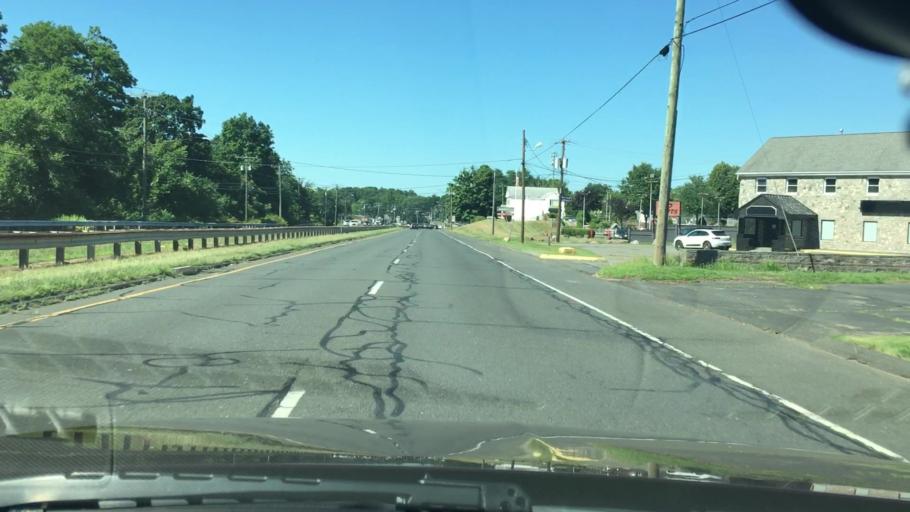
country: US
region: Connecticut
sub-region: Hartford County
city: Kensington
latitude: 41.6086
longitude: -72.7557
